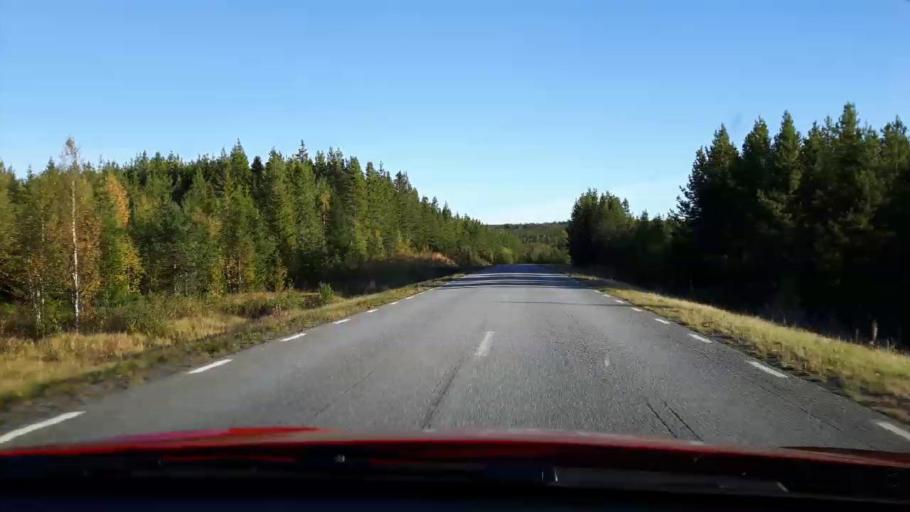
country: SE
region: Jaemtland
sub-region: OEstersunds Kommun
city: Lit
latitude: 63.7704
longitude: 14.7188
